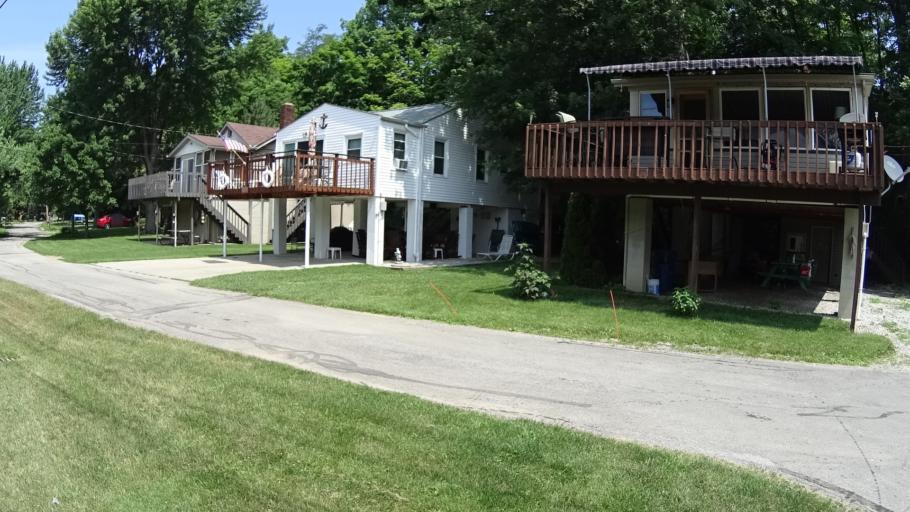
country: US
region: Ohio
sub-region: Lorain County
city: Vermilion
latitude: 41.4152
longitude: -82.3469
